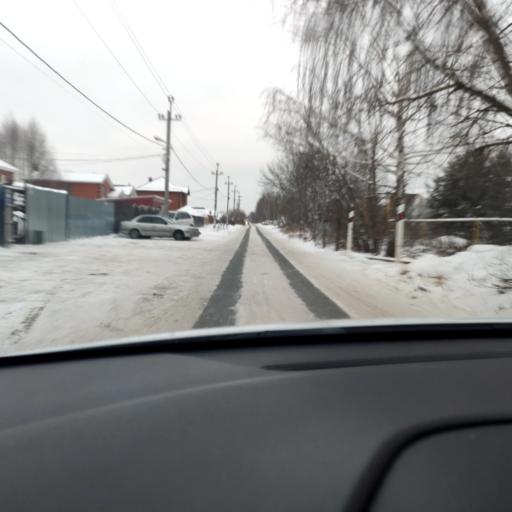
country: RU
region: Tatarstan
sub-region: Gorod Kazan'
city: Kazan
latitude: 55.8711
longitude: 49.1500
